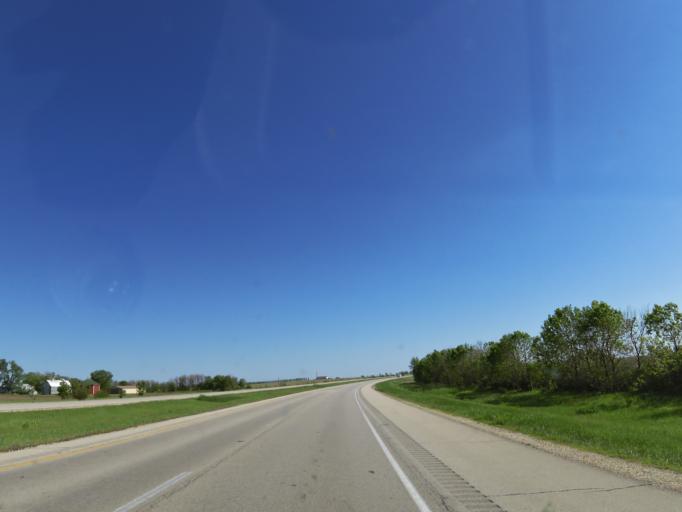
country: US
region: Illinois
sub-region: Ogle County
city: Rochelle
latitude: 41.8878
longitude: -89.0116
